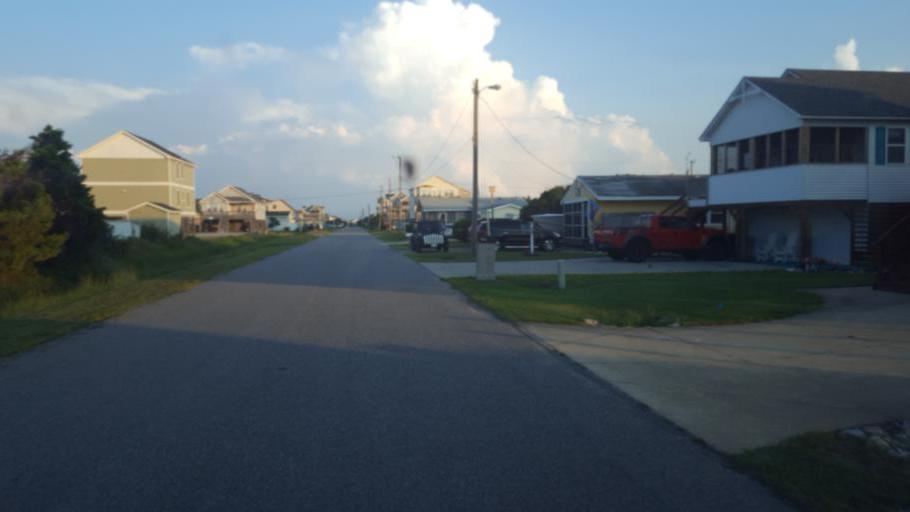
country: US
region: North Carolina
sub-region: Dare County
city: Kill Devil Hills
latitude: 36.0085
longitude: -75.6554
